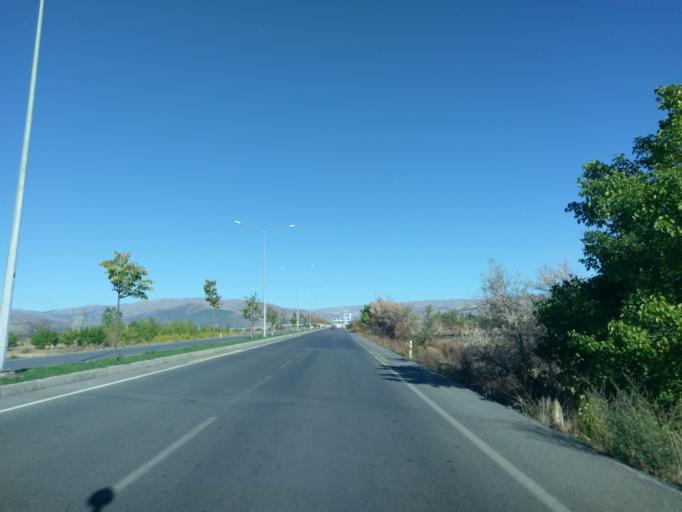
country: TR
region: Erzincan
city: Catalarmut
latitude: 39.7838
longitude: 39.4040
